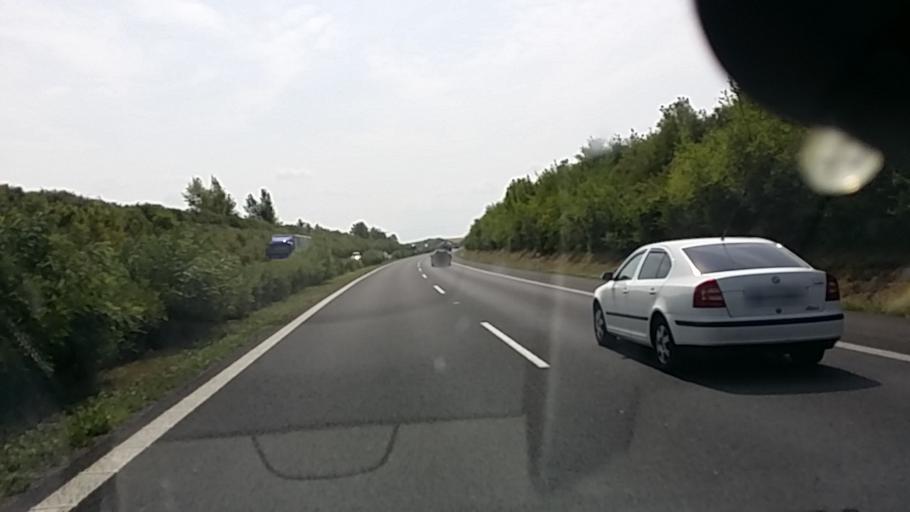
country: CZ
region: Ustecky
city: Bohusovice nad Ohri
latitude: 50.4656
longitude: 14.1062
